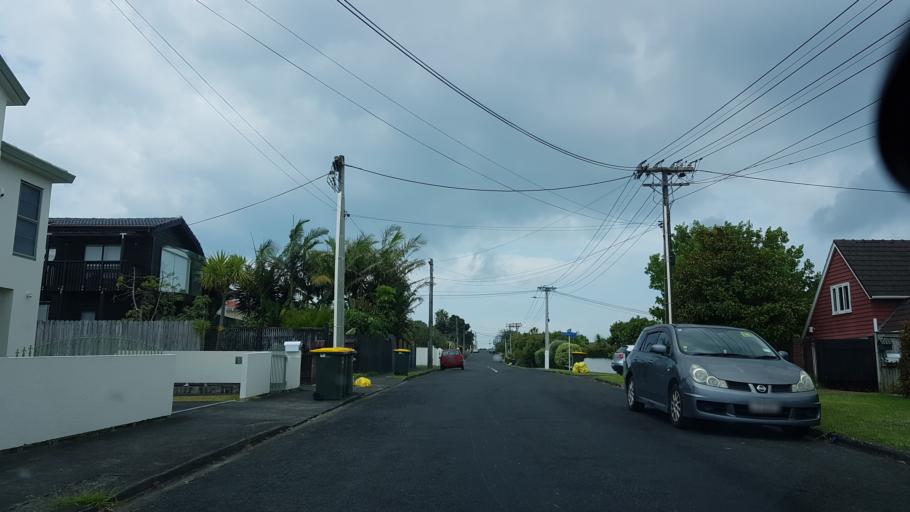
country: NZ
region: Auckland
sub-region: Auckland
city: North Shore
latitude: -36.8008
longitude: 174.7698
